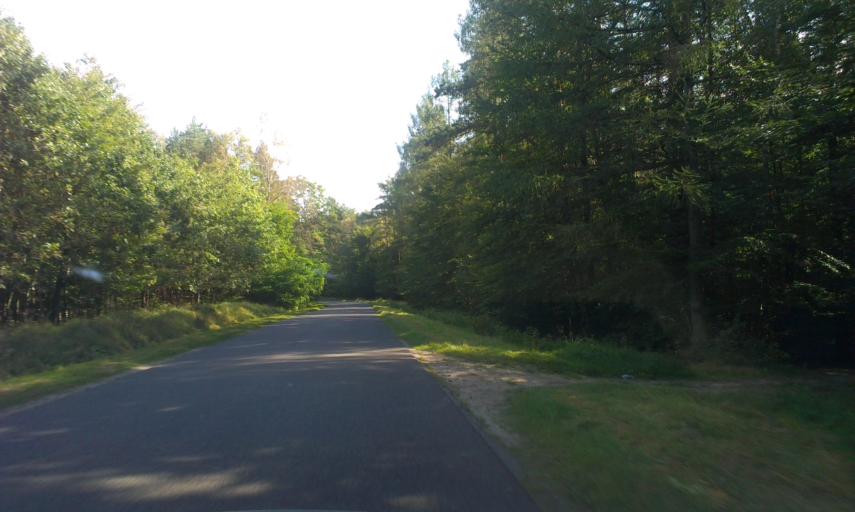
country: PL
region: Greater Poland Voivodeship
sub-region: Powiat zlotowski
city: Okonek
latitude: 53.5335
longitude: 16.9069
